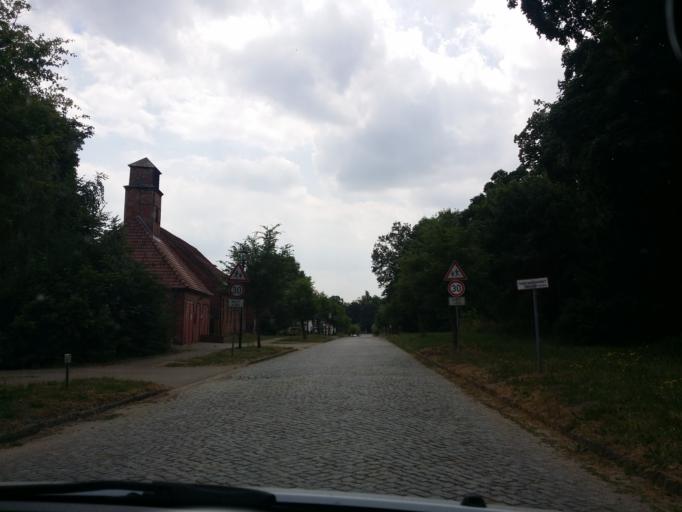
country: DE
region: Brandenburg
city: Gross Pankow
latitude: 53.0612
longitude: 12.0174
